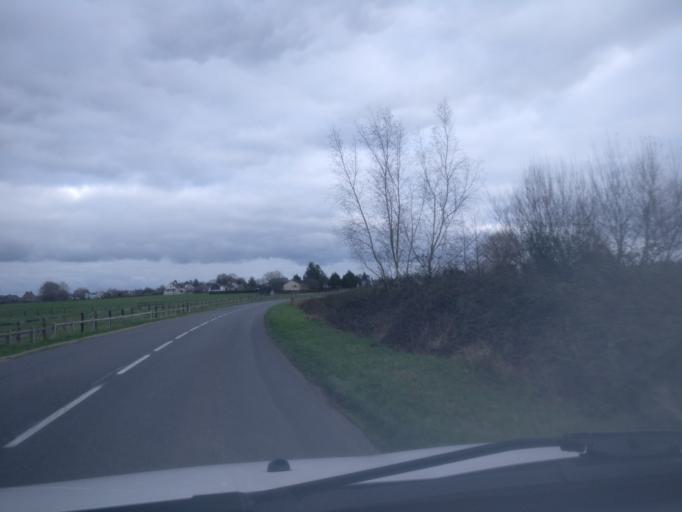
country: FR
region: Lower Normandy
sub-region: Departement de la Manche
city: Marcey-les-Greves
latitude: 48.6896
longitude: -1.3794
